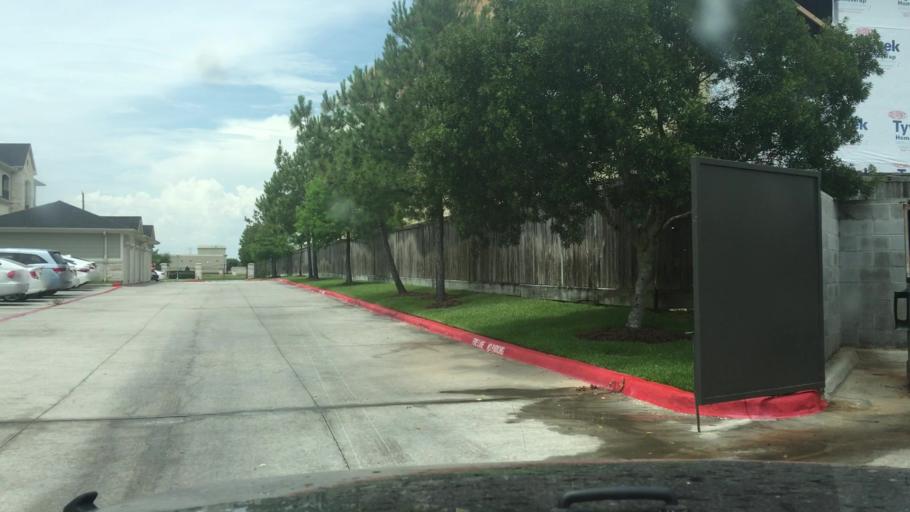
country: US
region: Texas
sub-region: Harris County
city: Humble
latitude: 29.9331
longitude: -95.2442
